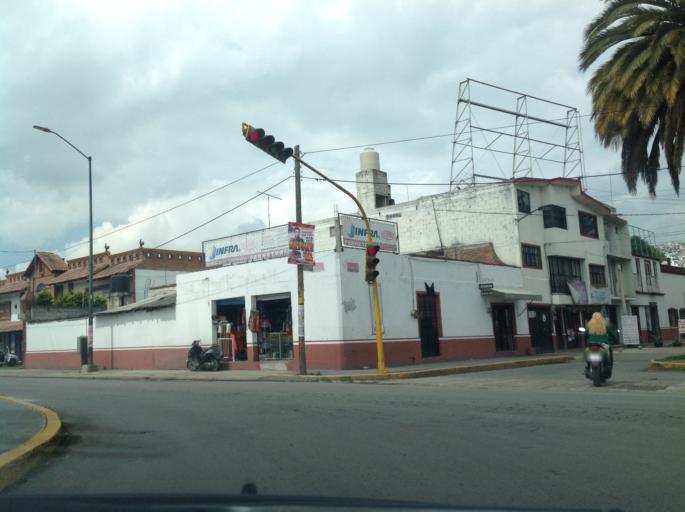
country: MX
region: Morelos
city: Tenango de Arista
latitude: 19.1053
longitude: -99.5866
